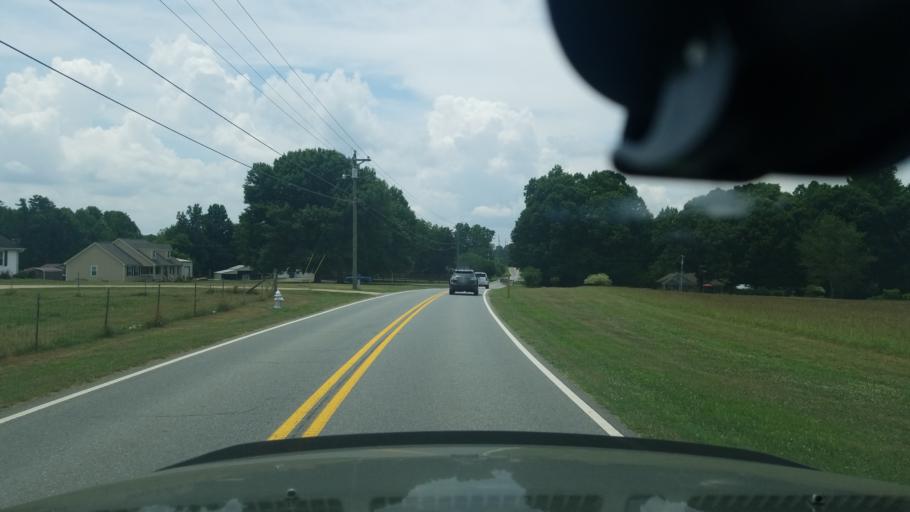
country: US
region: Georgia
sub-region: Fulton County
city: Milton
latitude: 34.1944
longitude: -84.2432
